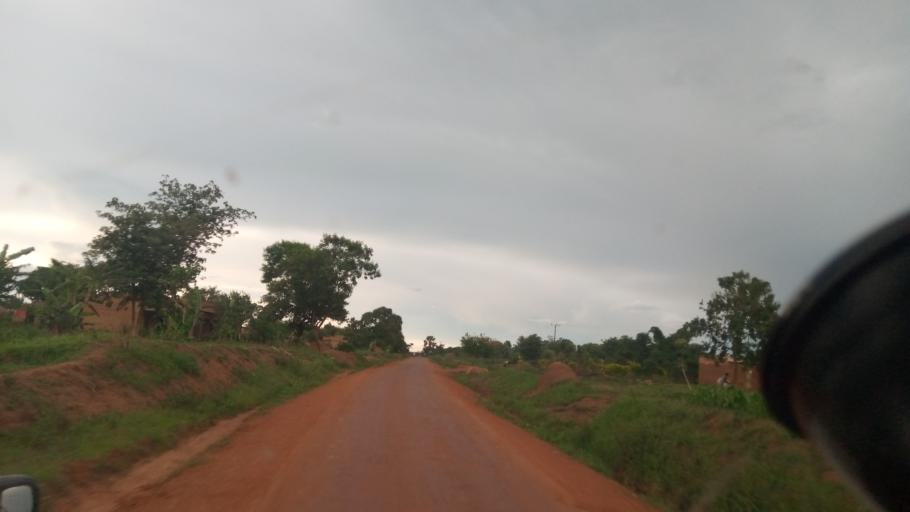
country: UG
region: Northern Region
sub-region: Kole District
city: Kole
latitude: 2.4661
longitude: 32.9363
